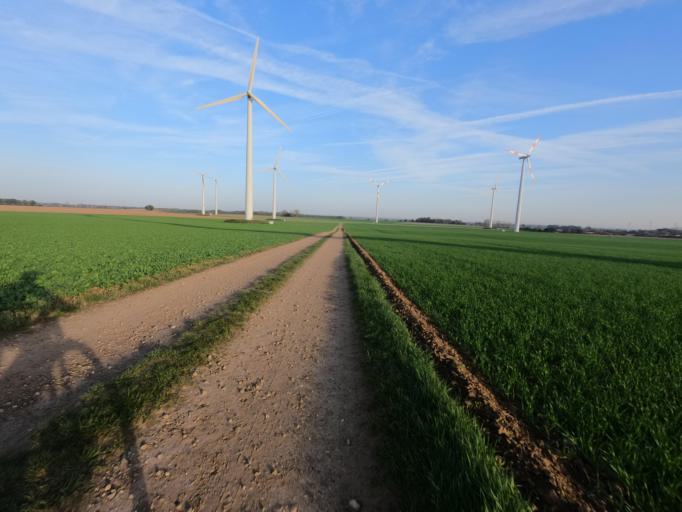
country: DE
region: North Rhine-Westphalia
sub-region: Regierungsbezirk Koln
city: Titz
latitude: 51.0426
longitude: 6.3782
